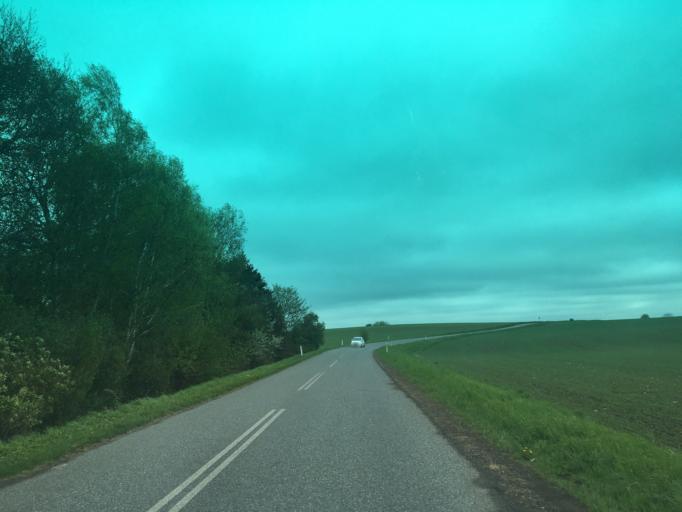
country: DK
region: Zealand
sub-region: Ringsted Kommune
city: Ringsted
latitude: 55.4363
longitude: 11.7163
